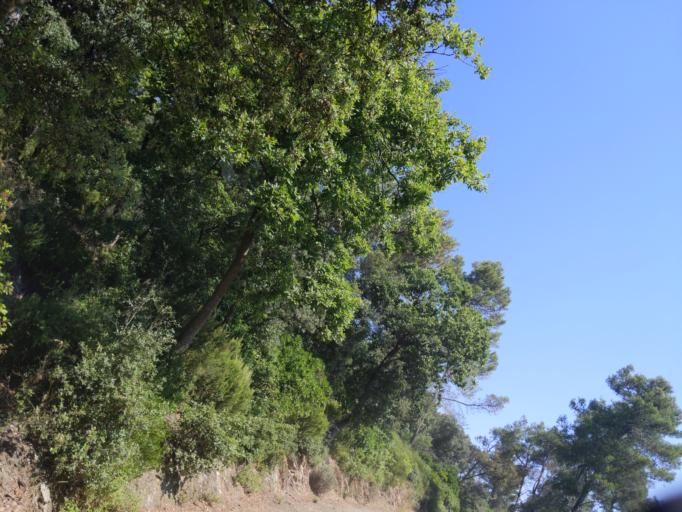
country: ES
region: Catalonia
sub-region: Provincia de Barcelona
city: Cerdanyola del Valles
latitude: 41.4584
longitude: 2.1364
